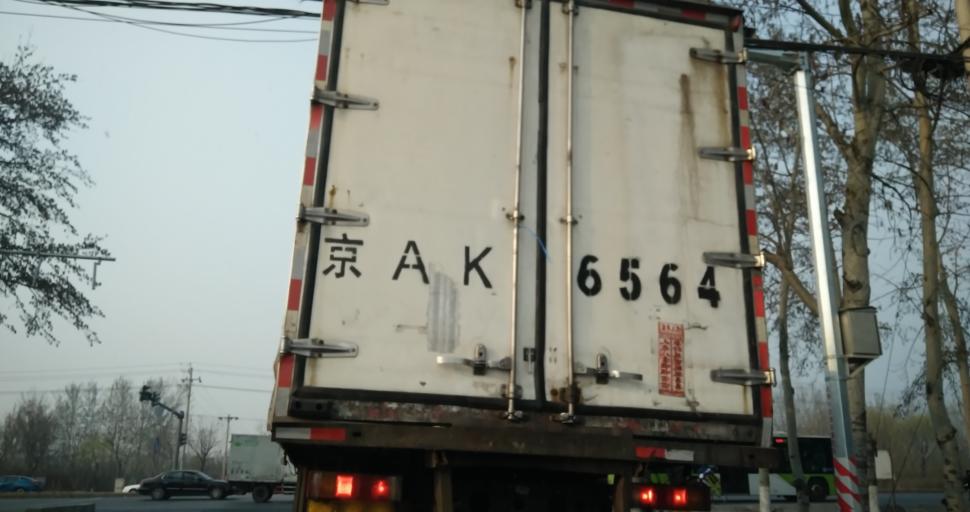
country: CN
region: Beijing
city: Xingfeng
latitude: 39.7203
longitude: 116.3601
